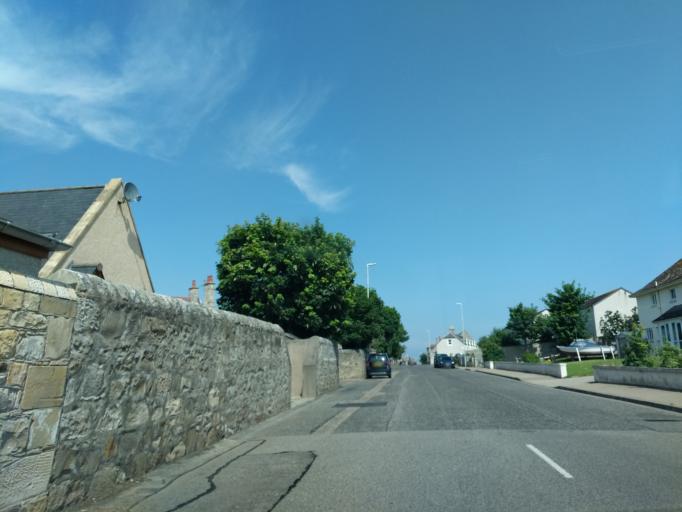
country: GB
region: Scotland
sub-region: Moray
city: Lossiemouth
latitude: 57.7178
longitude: -3.3016
